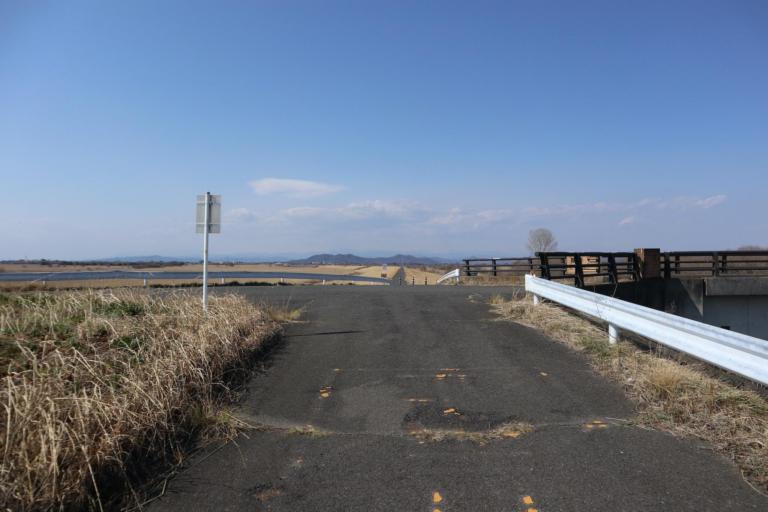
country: JP
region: Tochigi
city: Fujioka
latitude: 36.2378
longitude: 139.6830
